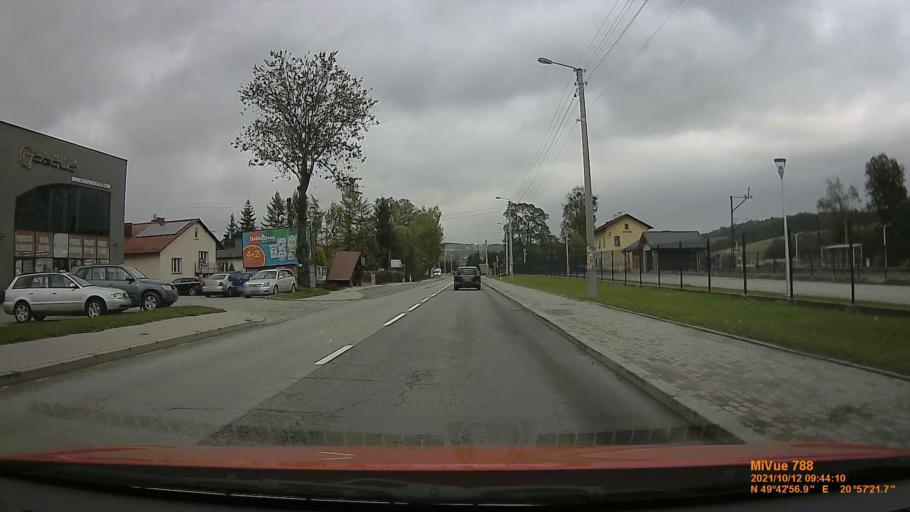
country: PL
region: Lesser Poland Voivodeship
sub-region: Powiat gorlicki
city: Bobowa
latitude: 49.7159
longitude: 20.9561
